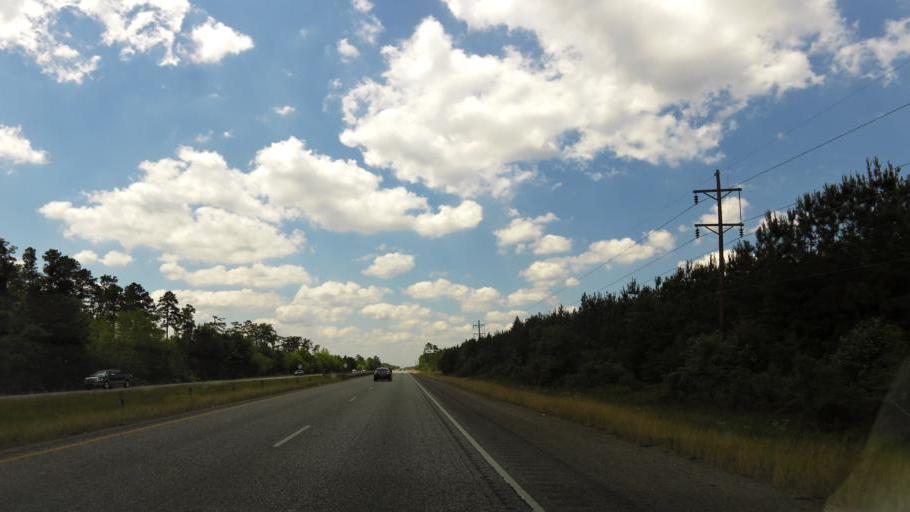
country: US
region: Texas
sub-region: Liberty County
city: Cleveland
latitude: 30.3979
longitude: -95.0572
